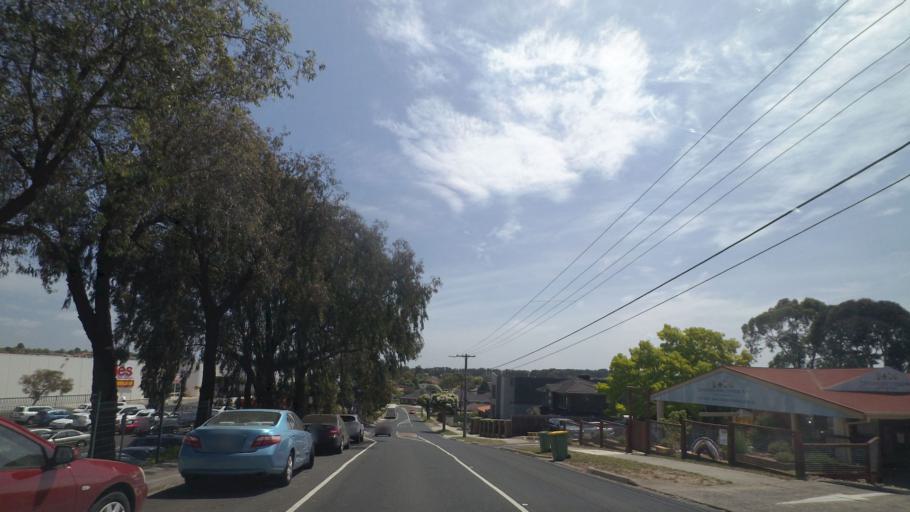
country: AU
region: Victoria
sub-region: Yarra Ranges
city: Chirnside Park
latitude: -37.7555
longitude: 145.3137
